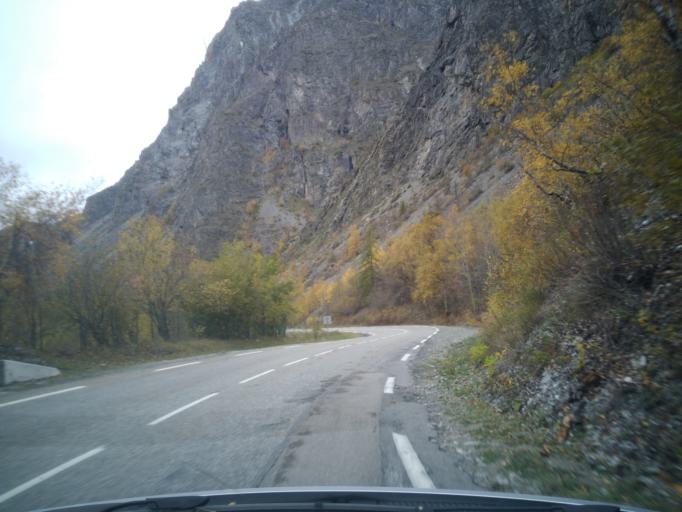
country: FR
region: Rhone-Alpes
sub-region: Departement de l'Isere
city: Mont-de-Lans
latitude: 45.0365
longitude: 6.2158
